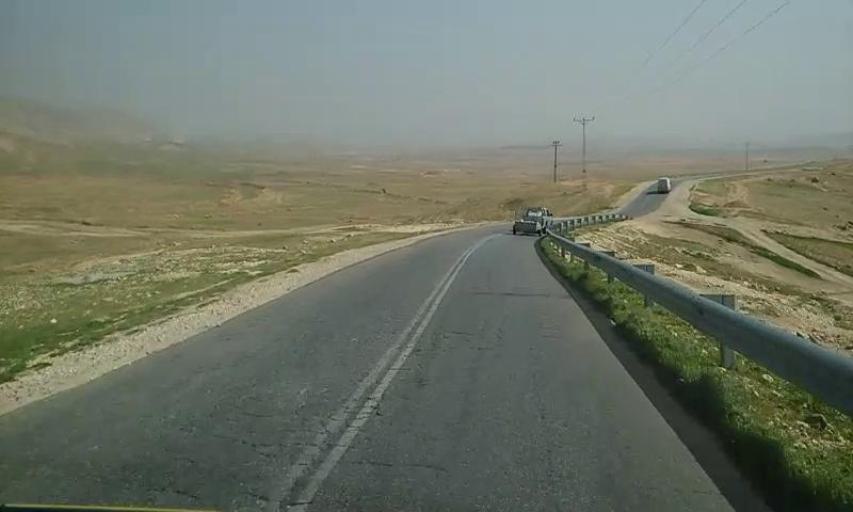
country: PS
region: West Bank
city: An Nuway`imah
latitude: 31.9190
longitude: 35.3904
